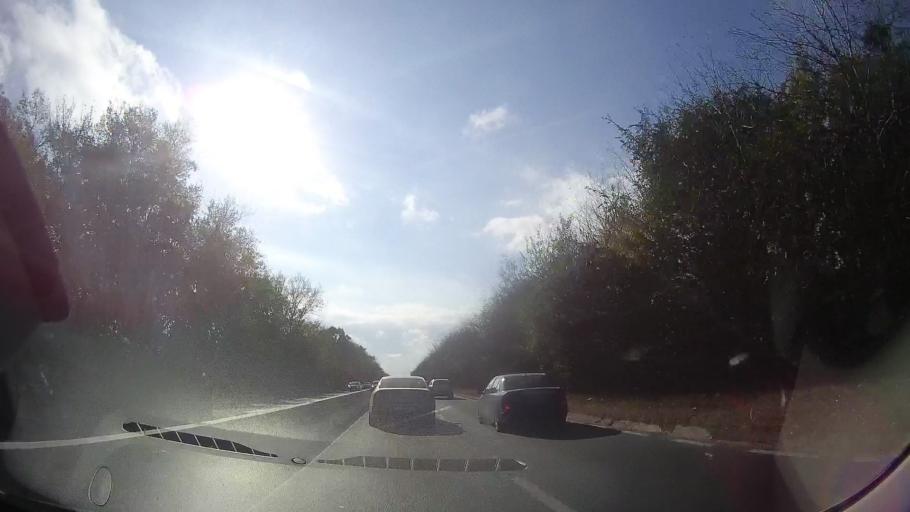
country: RO
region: Constanta
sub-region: Comuna Agigea
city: Agigea
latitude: 44.1280
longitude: 28.6158
